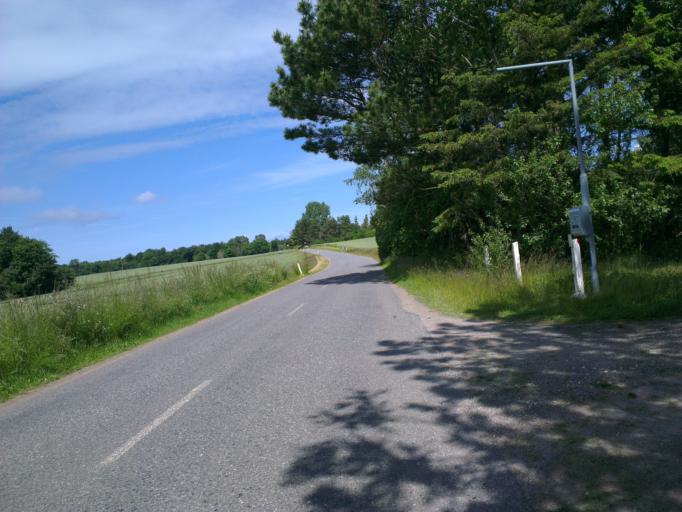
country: DK
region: Capital Region
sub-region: Frederikssund Kommune
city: Jaegerspris
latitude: 55.8088
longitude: 11.9326
